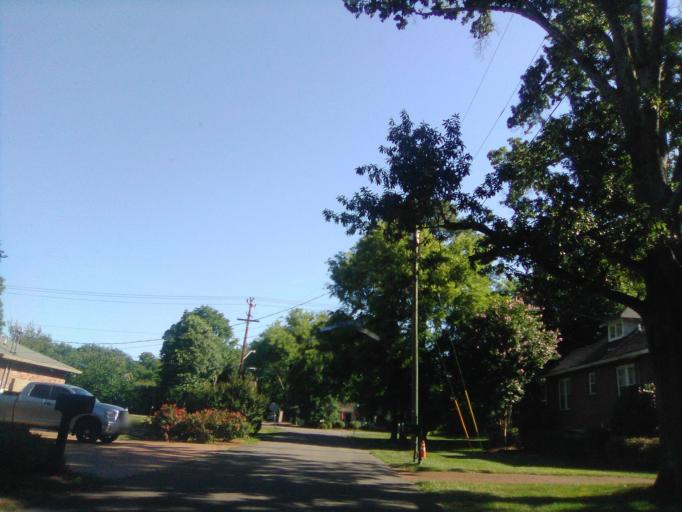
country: US
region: Tennessee
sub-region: Davidson County
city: Belle Meade
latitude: 36.1182
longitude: -86.8386
